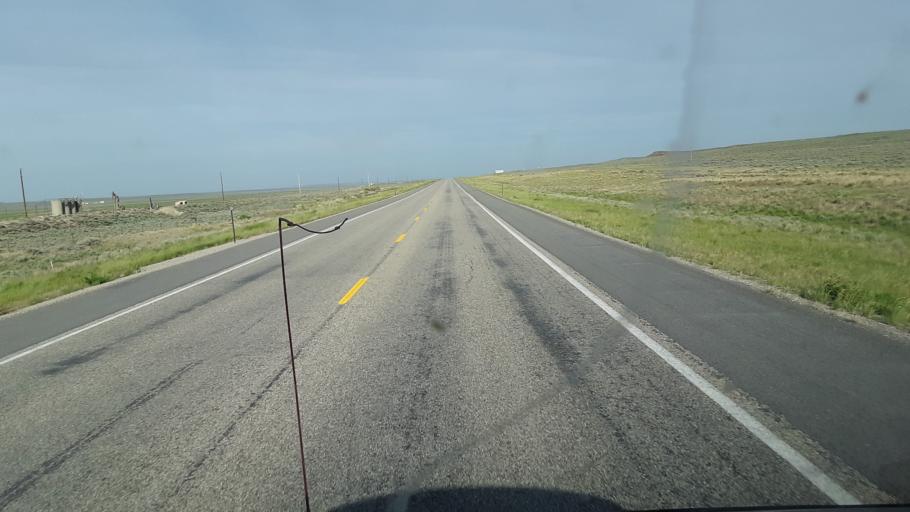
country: US
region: Wyoming
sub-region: Hot Springs County
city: Thermopolis
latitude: 43.1416
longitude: -107.5357
